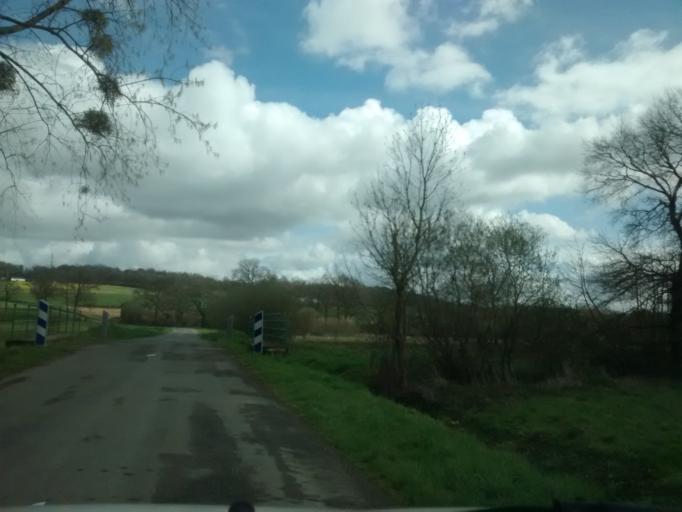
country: FR
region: Brittany
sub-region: Departement d'Ille-et-Vilaine
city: Livre-sur-Changeon
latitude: 48.2015
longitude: -1.3601
